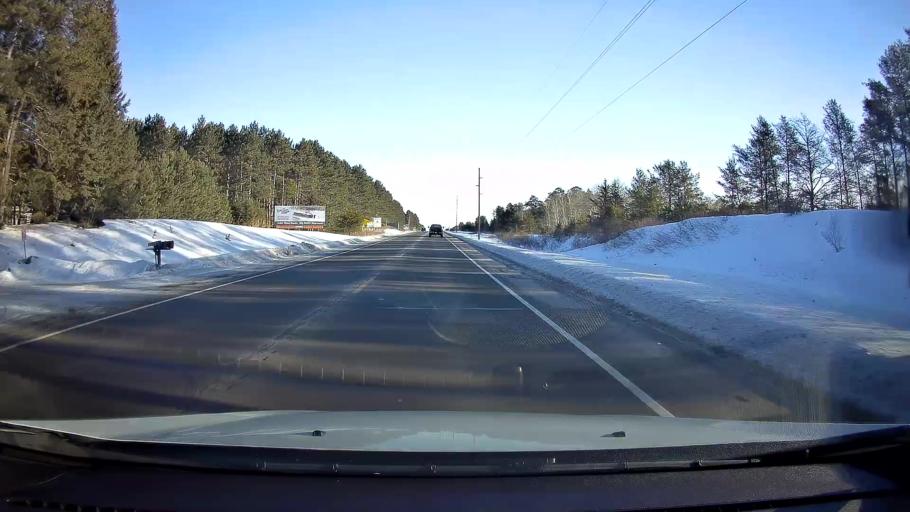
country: US
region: Wisconsin
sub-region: Sawyer County
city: Hayward
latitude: 45.9941
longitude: -91.5136
